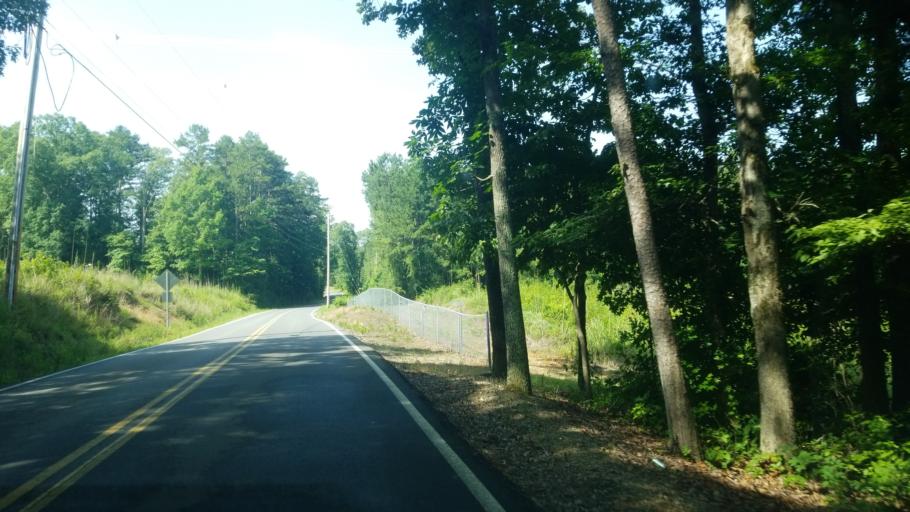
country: US
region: Tennessee
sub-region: Hamilton County
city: Collegedale
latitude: 35.0818
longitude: -84.9947
